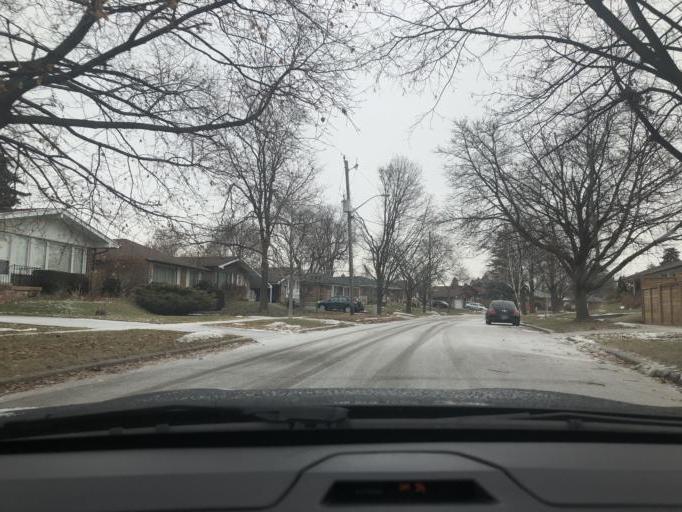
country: CA
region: Ontario
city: Scarborough
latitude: 43.7808
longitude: -79.2734
